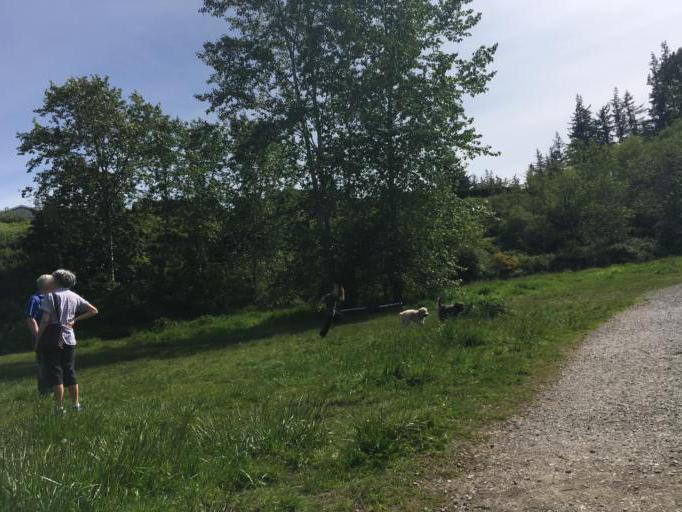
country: US
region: Washington
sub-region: Whatcom County
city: Bellingham
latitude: 48.7166
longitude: -122.5128
